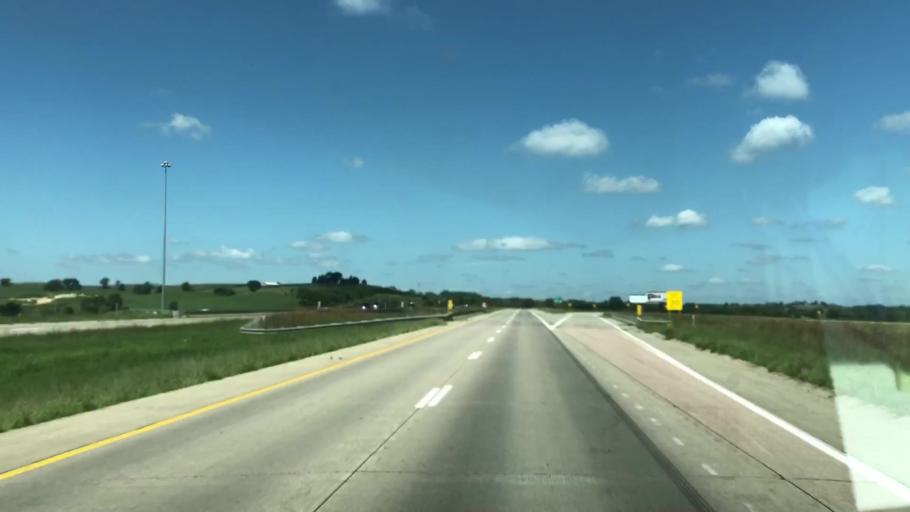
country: US
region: Iowa
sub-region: Woodbury County
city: Sioux City
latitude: 42.5465
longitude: -96.3405
